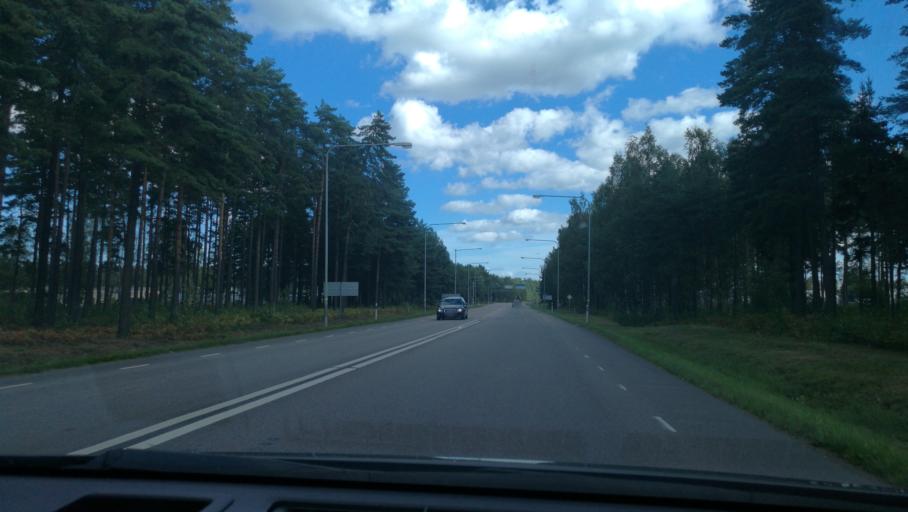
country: SE
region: Vaestra Goetaland
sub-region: Lidkopings Kommun
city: Lidkoping
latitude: 58.4892
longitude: 13.1878
